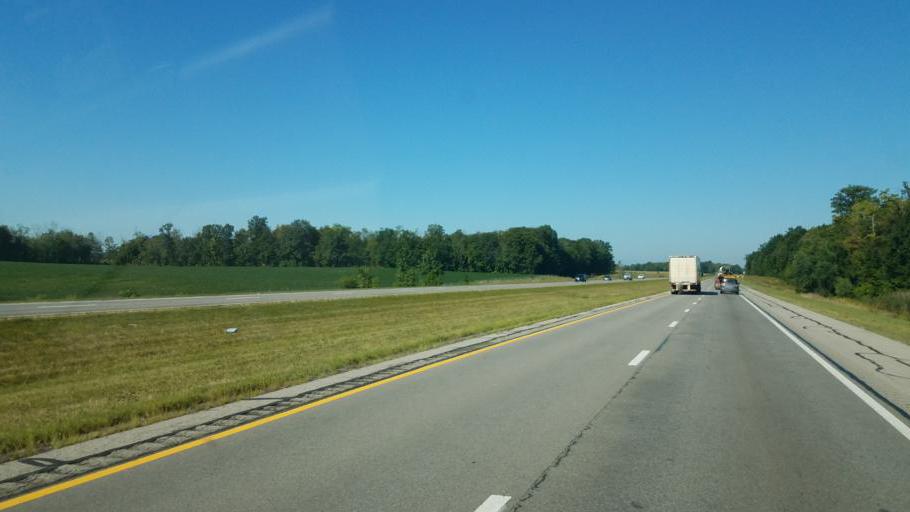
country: US
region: Ohio
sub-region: Crawford County
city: Crestline
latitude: 40.7619
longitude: -82.7040
